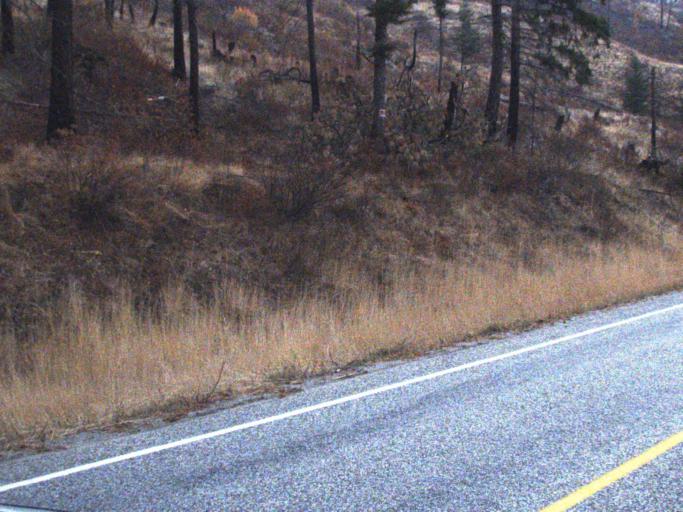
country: US
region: Washington
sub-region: Stevens County
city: Kettle Falls
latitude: 48.7565
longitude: -118.1353
